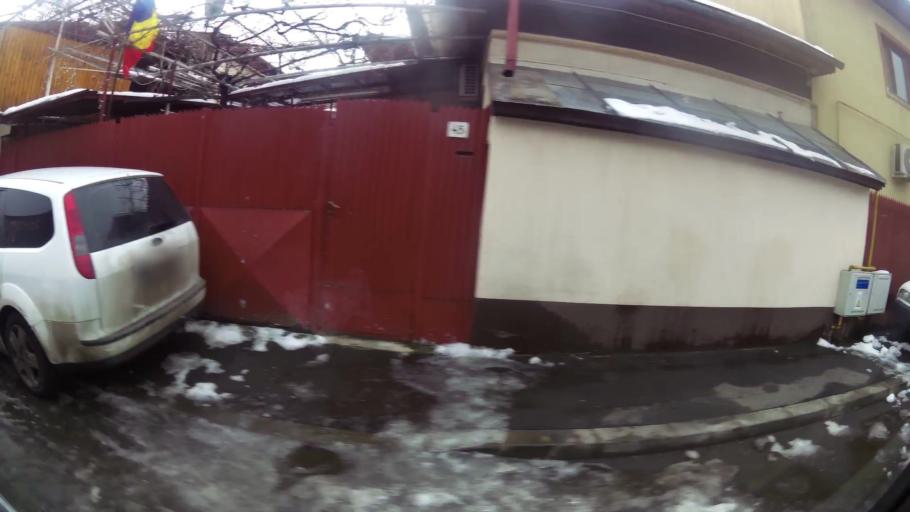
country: RO
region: Bucuresti
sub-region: Municipiul Bucuresti
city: Bucuresti
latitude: 44.4121
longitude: 26.0653
